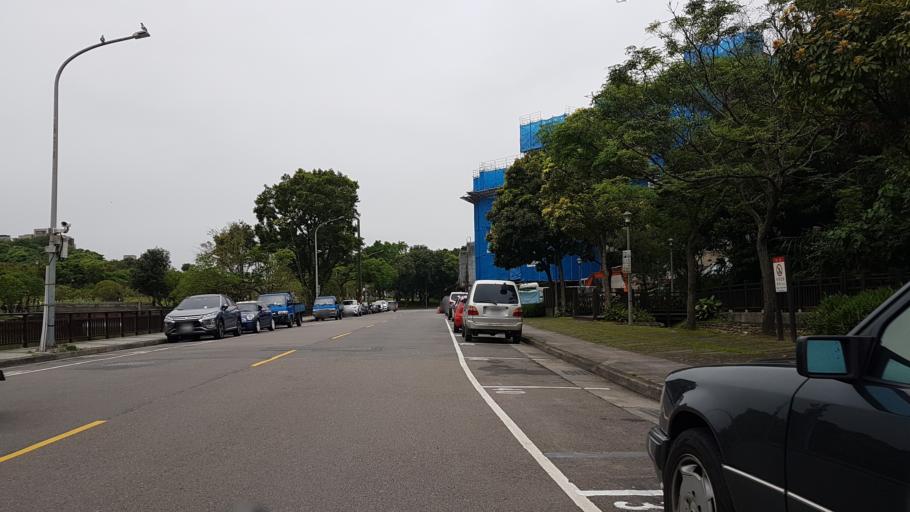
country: TW
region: Taipei
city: Taipei
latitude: 25.0424
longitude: 121.5929
